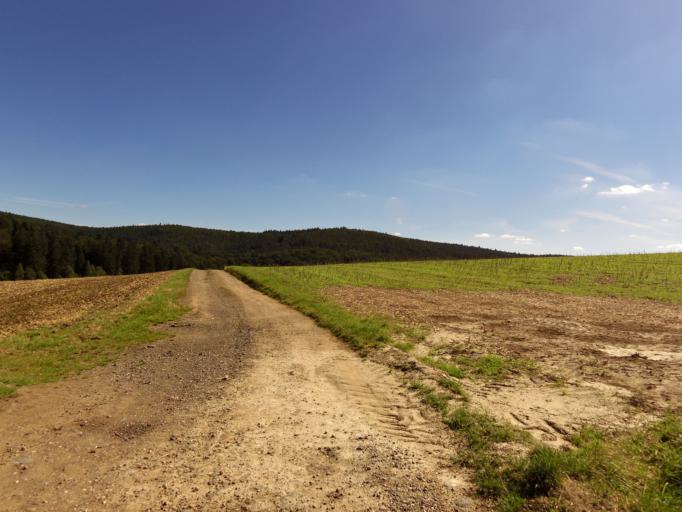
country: DE
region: Hesse
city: Reichelsheim
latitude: 49.6495
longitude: 8.8761
